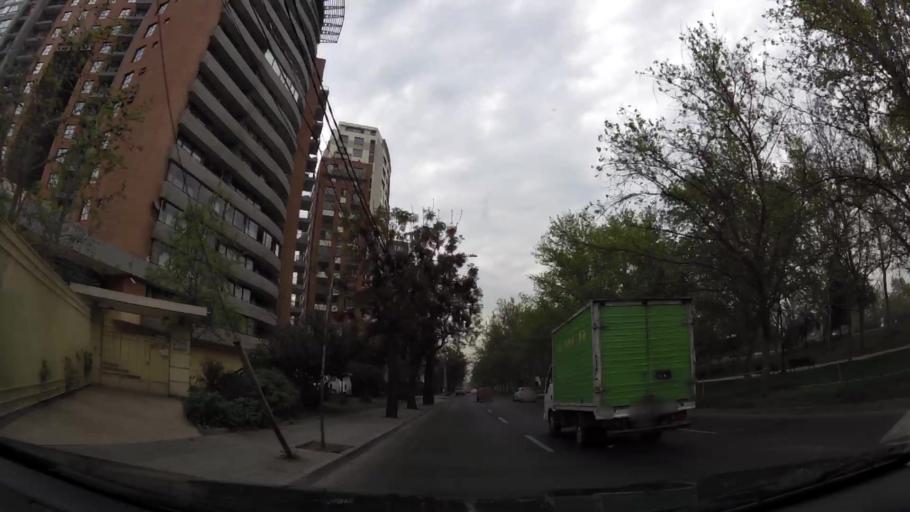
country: CL
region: Santiago Metropolitan
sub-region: Provincia de Santiago
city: Santiago
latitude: -33.4302
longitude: -70.6662
